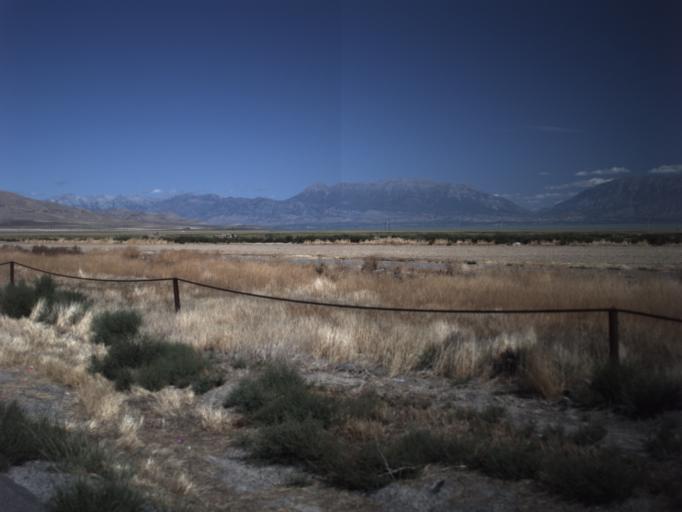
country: US
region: Utah
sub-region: Utah County
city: Genola
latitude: 40.1106
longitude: -111.9591
